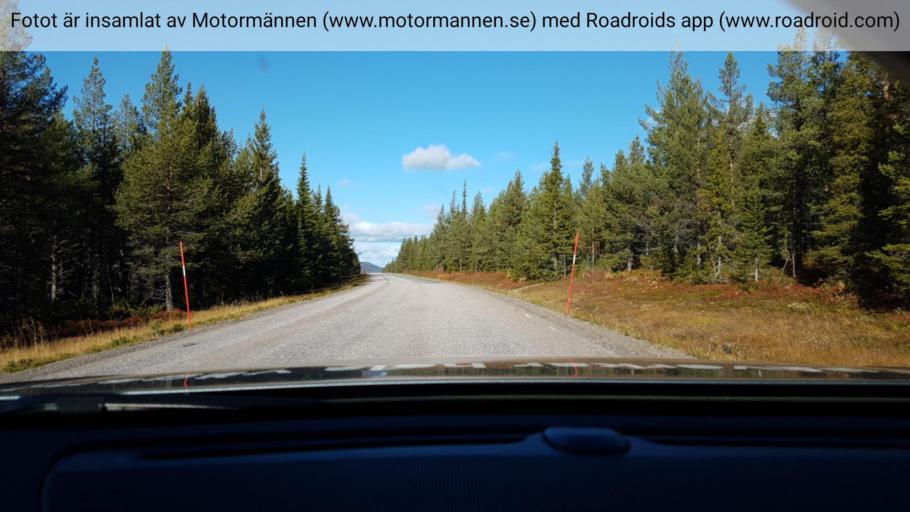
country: SE
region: Norrbotten
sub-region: Arjeplogs Kommun
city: Arjeplog
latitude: 65.8090
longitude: 18.4593
